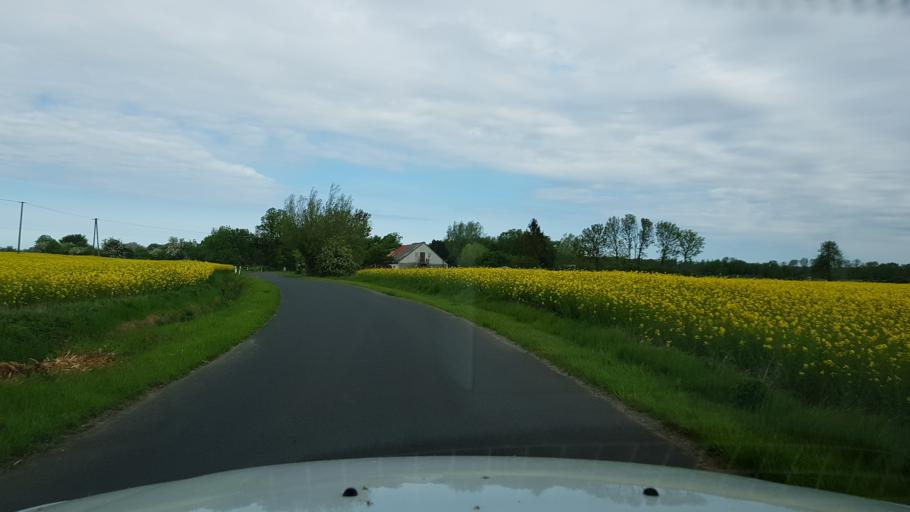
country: PL
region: West Pomeranian Voivodeship
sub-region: Powiat kolobrzeski
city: Ustronie Morskie
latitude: 54.2158
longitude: 15.8188
